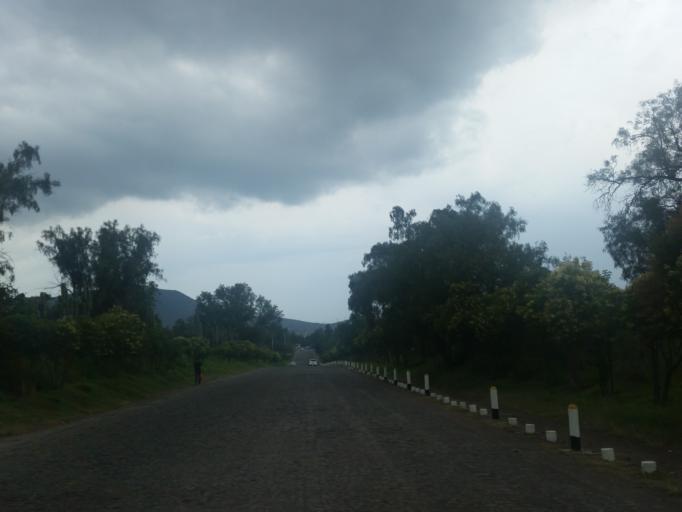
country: MX
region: Mexico
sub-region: Teotihuacan
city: Teotihuacan de Arista
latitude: 19.6868
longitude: -98.8427
